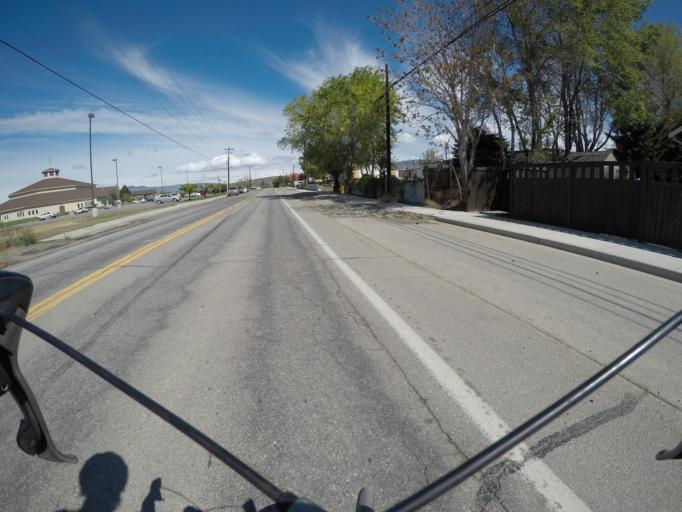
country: US
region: Washington
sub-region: Chelan County
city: South Wenatchee
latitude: 47.3966
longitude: -120.2603
